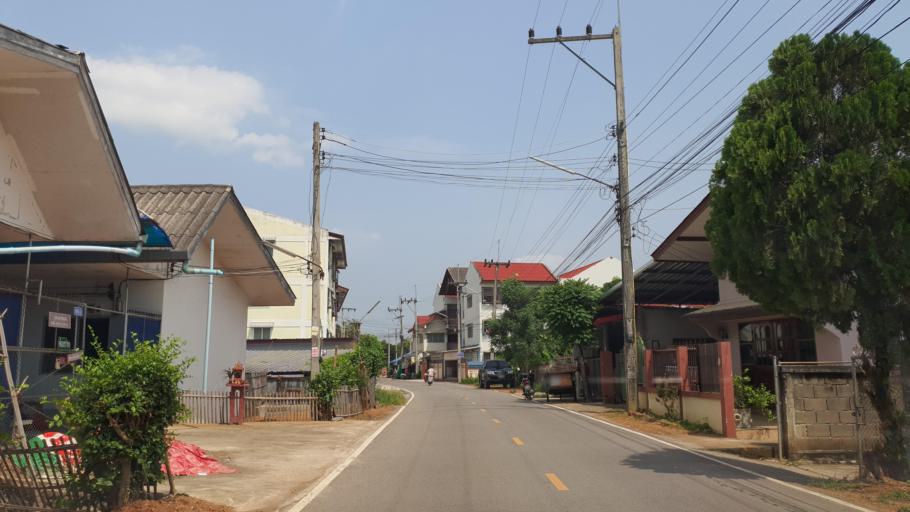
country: TH
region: Lamphun
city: Lamphun
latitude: 18.6023
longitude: 99.0284
